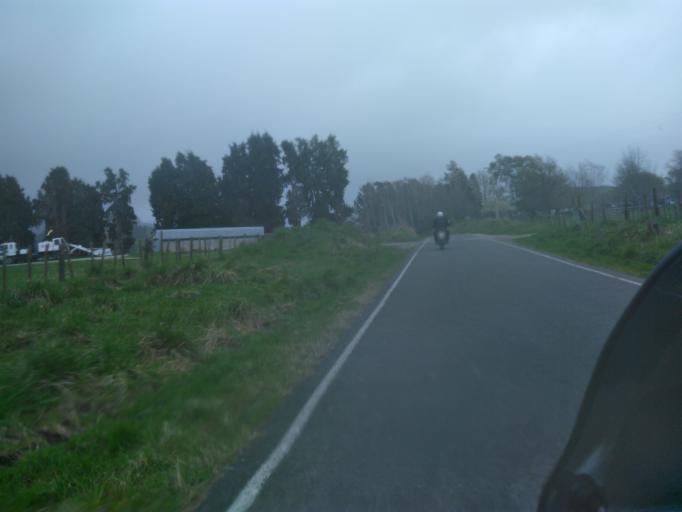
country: NZ
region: Gisborne
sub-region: Gisborne District
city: Gisborne
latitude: -38.6598
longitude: 177.7201
